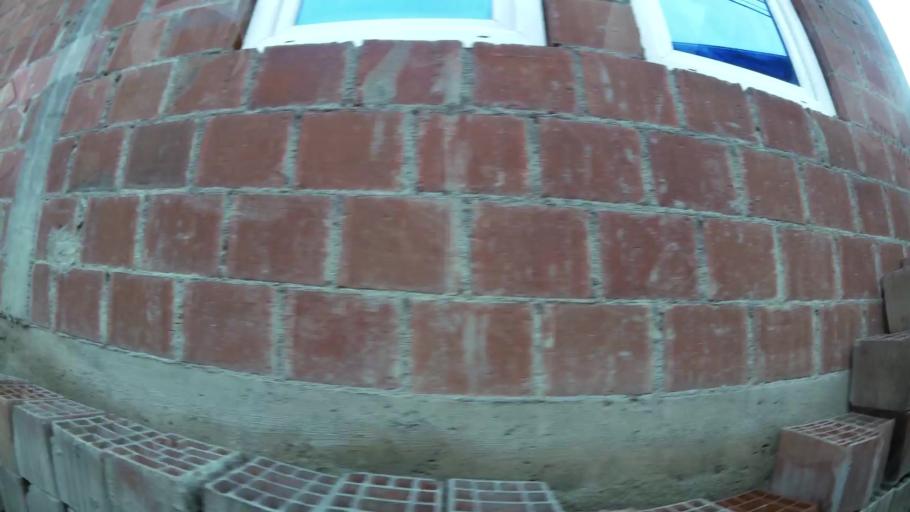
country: XK
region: Pristina
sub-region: Komuna e Prishtines
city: Pristina
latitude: 42.6806
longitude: 21.1650
